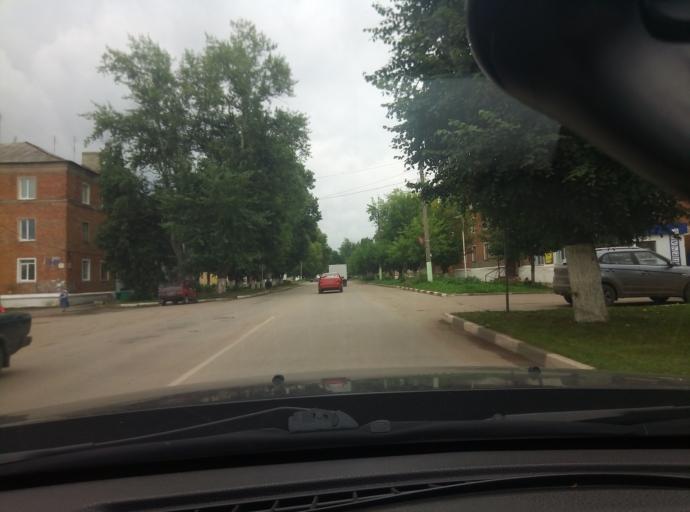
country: RU
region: Tula
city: Kimovsk
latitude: 53.9719
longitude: 38.5328
